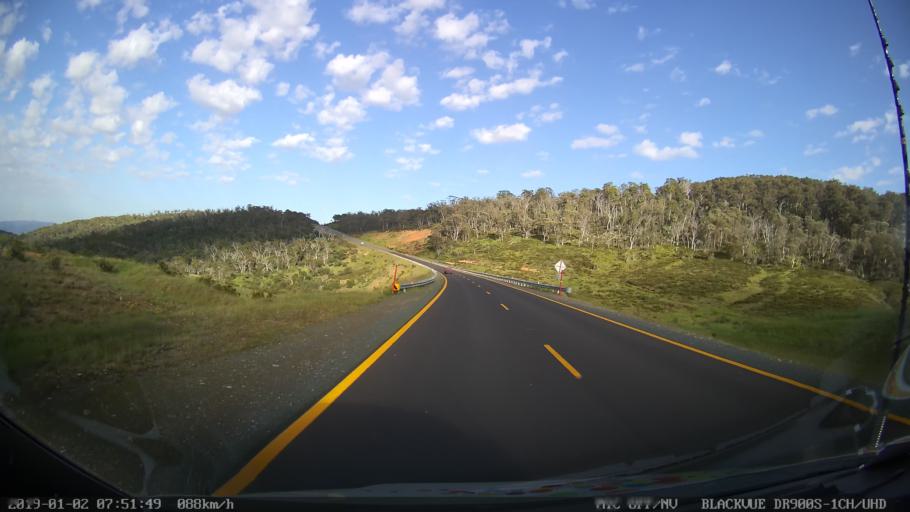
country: AU
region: New South Wales
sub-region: Tumut Shire
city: Tumut
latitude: -35.7147
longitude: 148.5276
